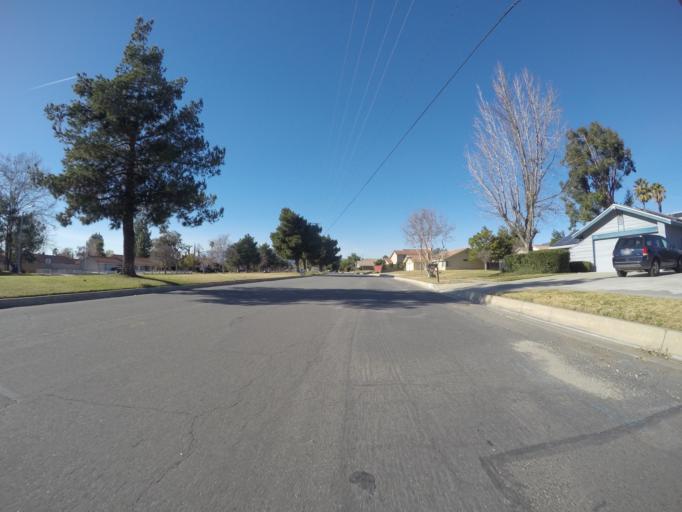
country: US
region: California
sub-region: San Bernardino County
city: Muscoy
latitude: 34.1389
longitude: -117.3712
